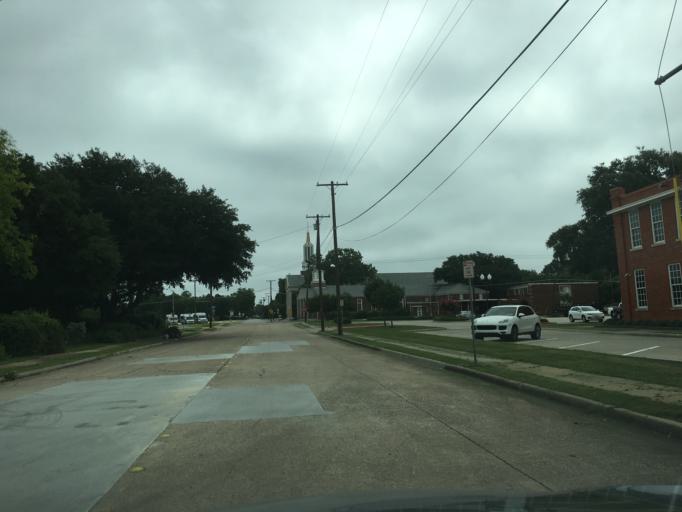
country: US
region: Texas
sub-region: Dallas County
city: Richardson
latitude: 32.9459
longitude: -96.7329
